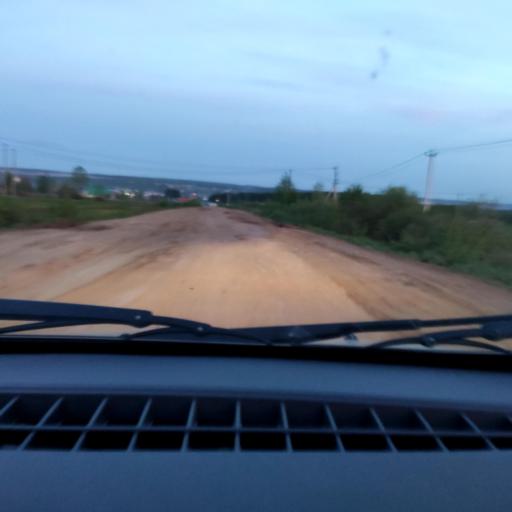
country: RU
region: Bashkortostan
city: Iglino
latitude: 54.8465
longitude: 56.4018
